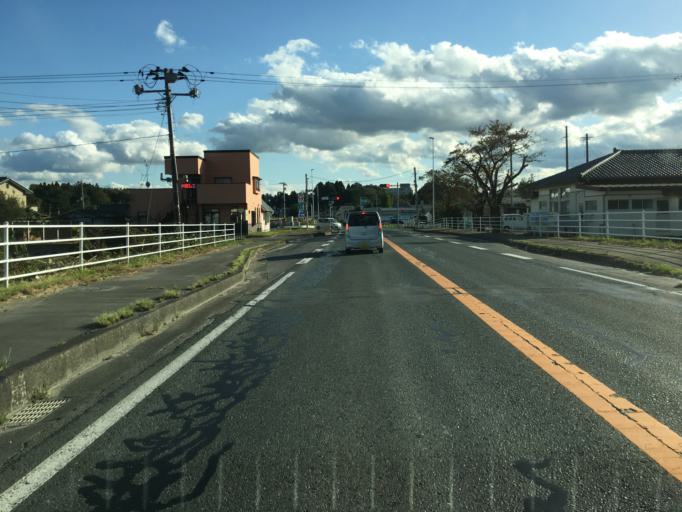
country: JP
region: Miyagi
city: Marumori
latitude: 37.8699
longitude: 140.9193
